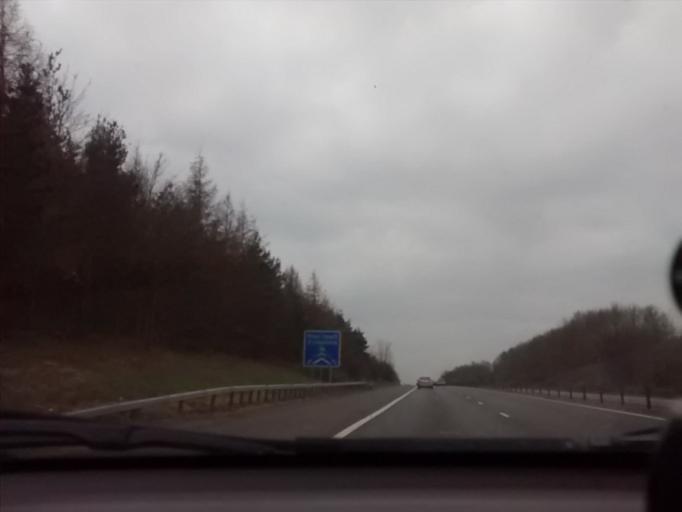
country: GB
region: England
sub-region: Essex
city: Saffron Walden
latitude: 51.9952
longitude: 0.1951
